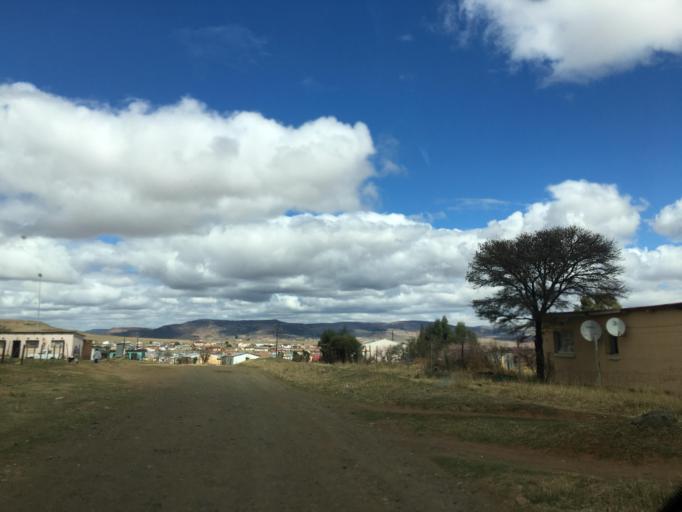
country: ZA
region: Eastern Cape
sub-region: Chris Hani District Municipality
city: Cala
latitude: -31.5304
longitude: 27.7025
